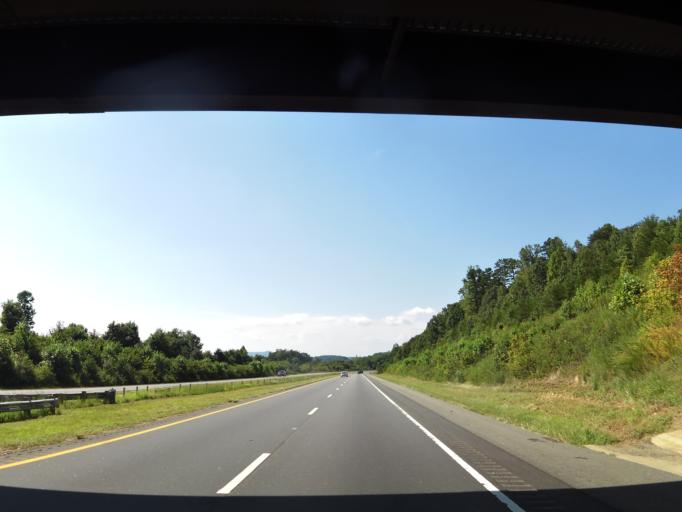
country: US
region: North Carolina
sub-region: Catawba County
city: Newton
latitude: 35.6164
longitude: -81.2827
